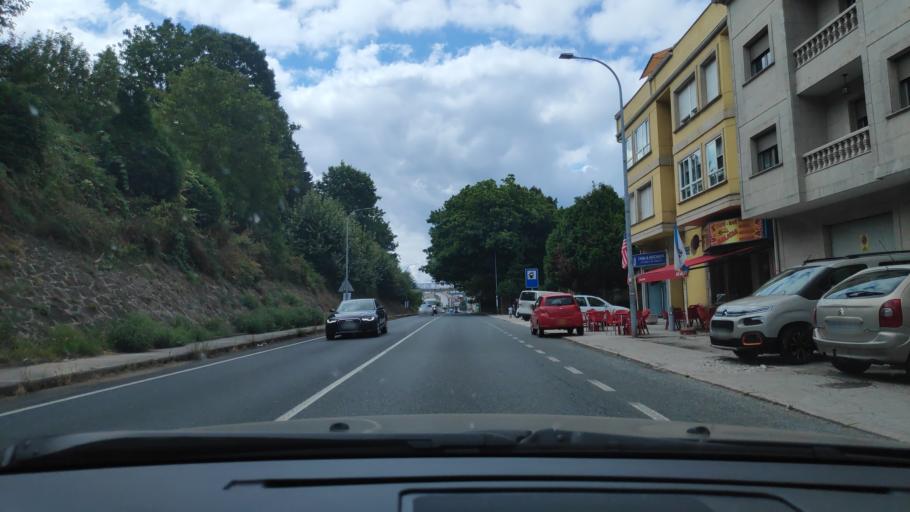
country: ES
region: Galicia
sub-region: Provincia da Coruna
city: Padron
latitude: 42.7224
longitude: -8.6508
